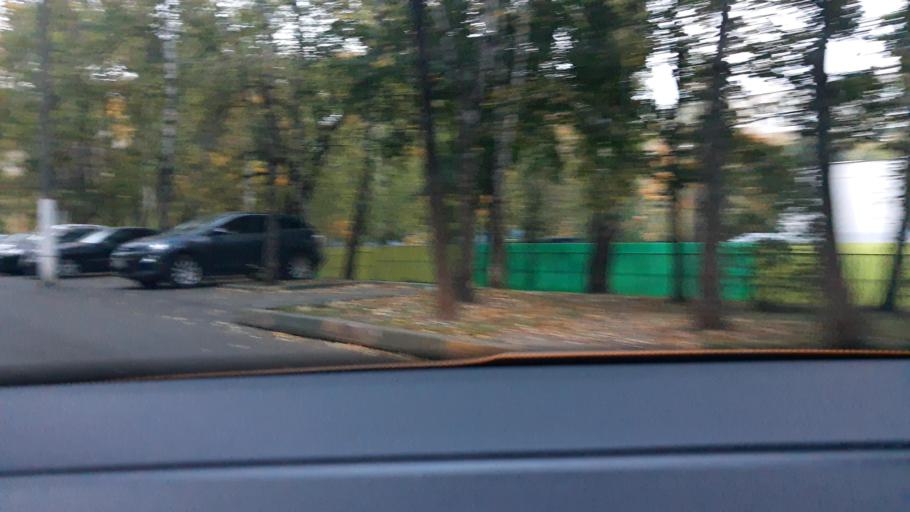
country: RU
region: Moscow
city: Otradnoye
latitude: 55.8698
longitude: 37.5970
